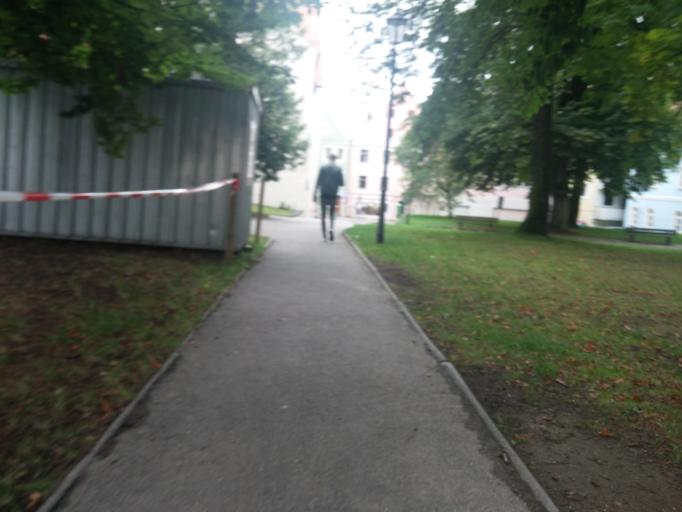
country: DE
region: Bavaria
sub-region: Swabia
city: Memmingen
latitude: 47.9856
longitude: 10.1788
